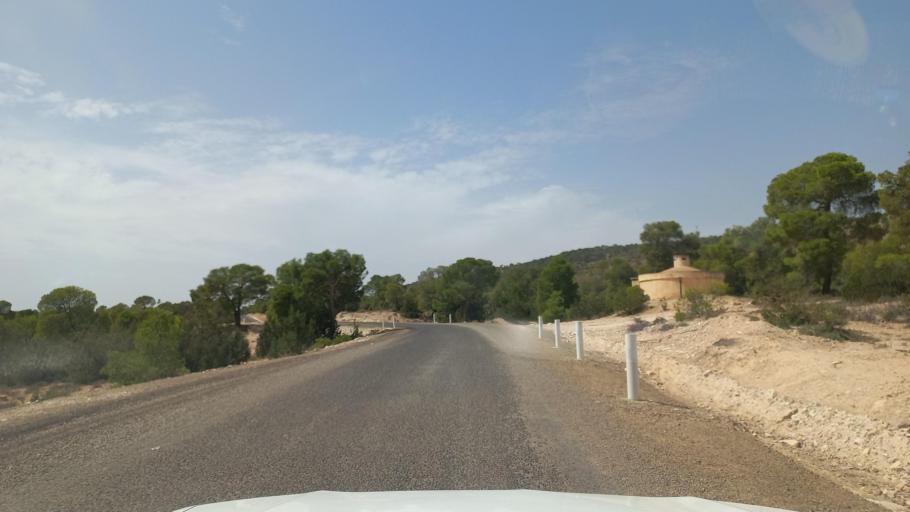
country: TN
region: Al Qasrayn
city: Sbiba
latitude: 35.3794
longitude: 8.9200
